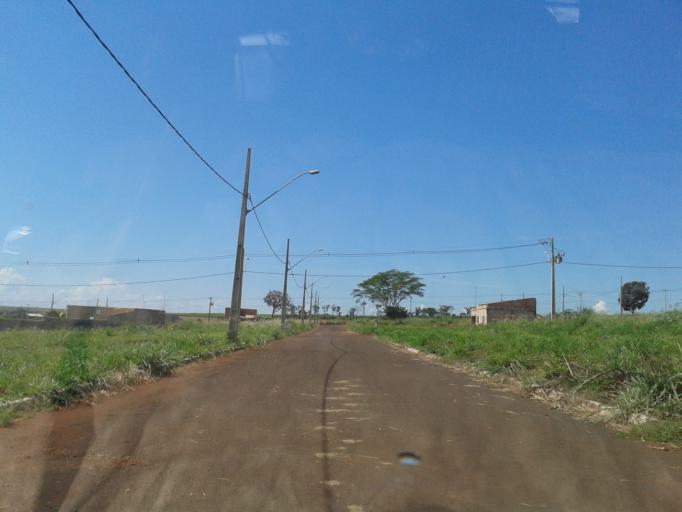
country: BR
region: Goias
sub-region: Itumbiara
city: Itumbiara
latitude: -18.4253
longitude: -49.1831
